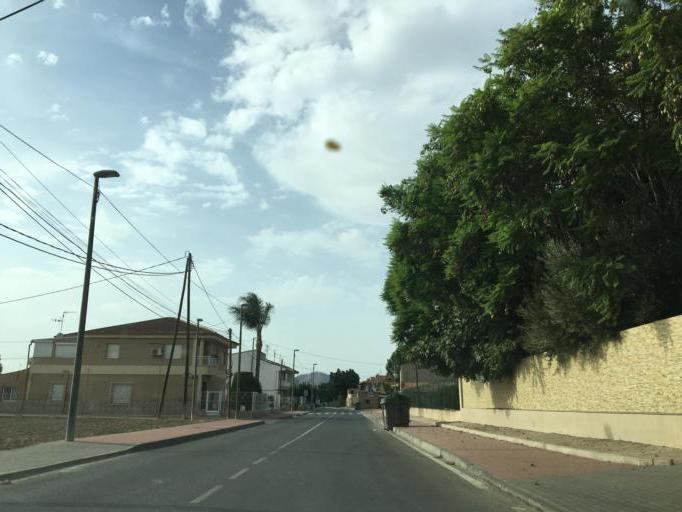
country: ES
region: Murcia
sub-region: Murcia
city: Murcia
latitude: 38.0064
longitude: -1.0791
